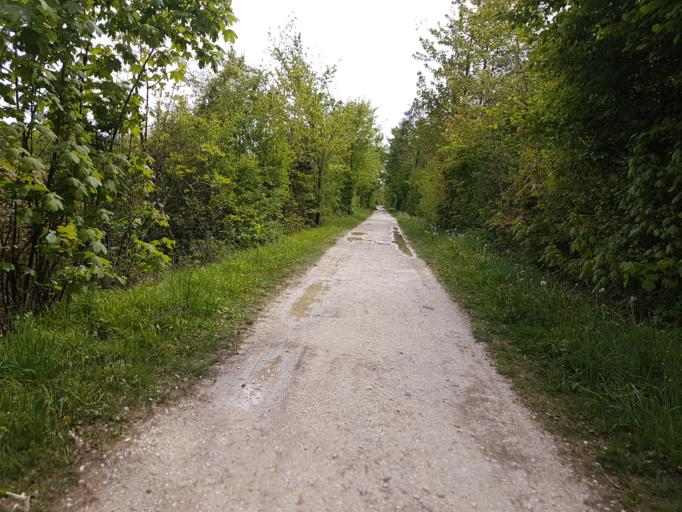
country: CH
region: Aargau
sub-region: Bezirk Brugg
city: Veltheim
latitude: 47.4298
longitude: 8.1608
